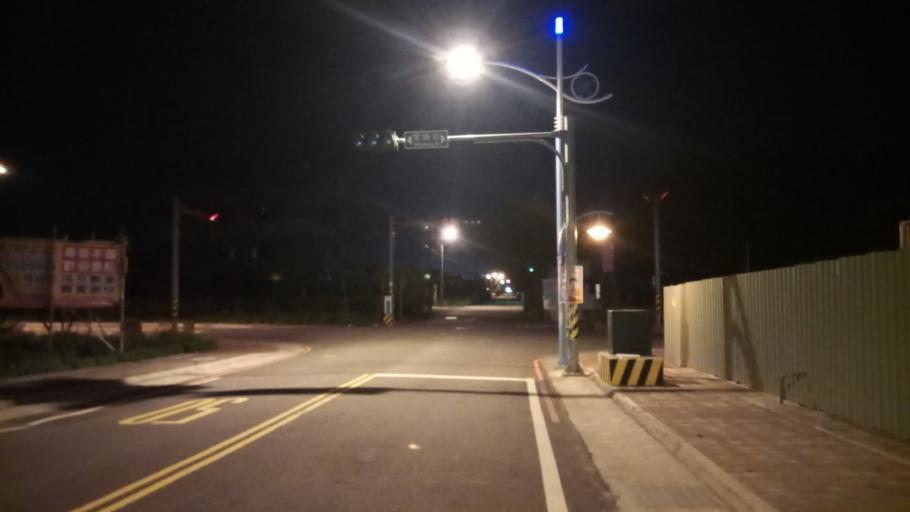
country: TW
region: Taiwan
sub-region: Hsinchu
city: Zhubei
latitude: 24.7796
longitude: 121.0738
